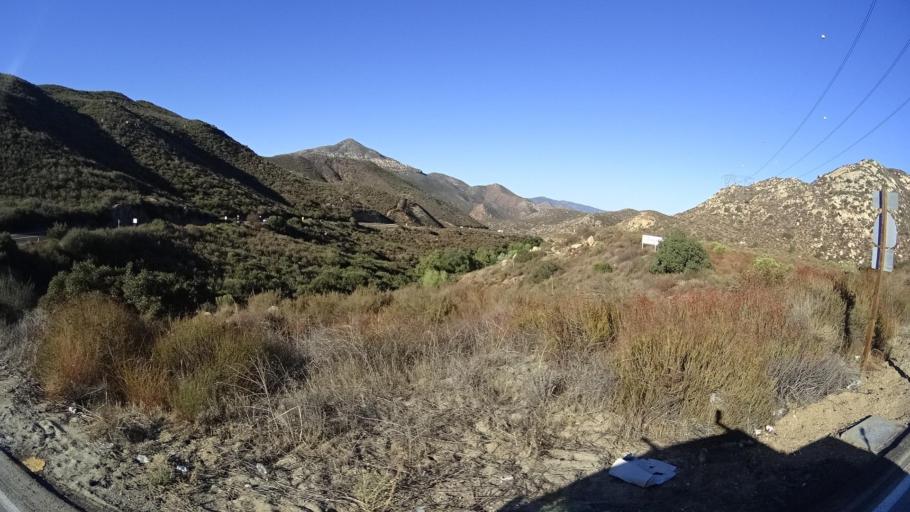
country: MX
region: Baja California
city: Tecate
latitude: 32.5985
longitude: -116.6431
